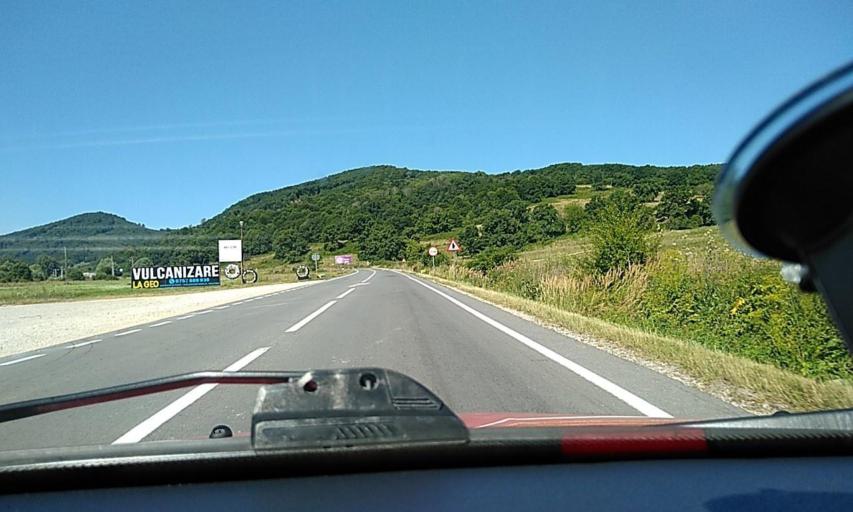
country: RO
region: Brasov
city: Maierus
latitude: 45.9060
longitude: 25.4950
